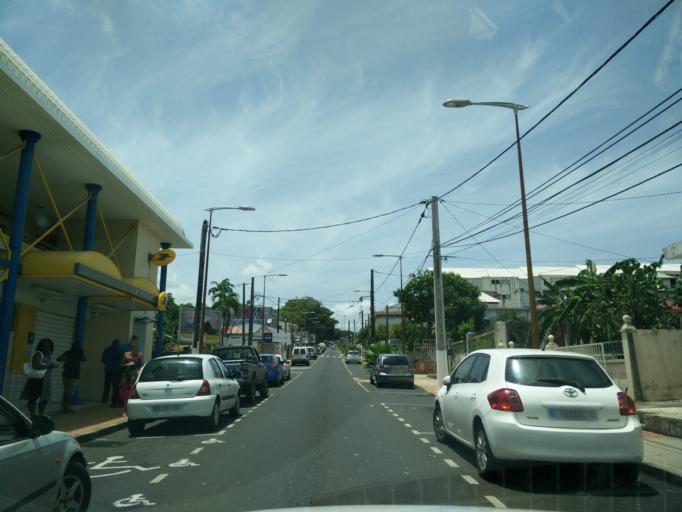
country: GP
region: Guadeloupe
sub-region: Guadeloupe
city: Petit-Bourg
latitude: 16.1937
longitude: -61.5925
